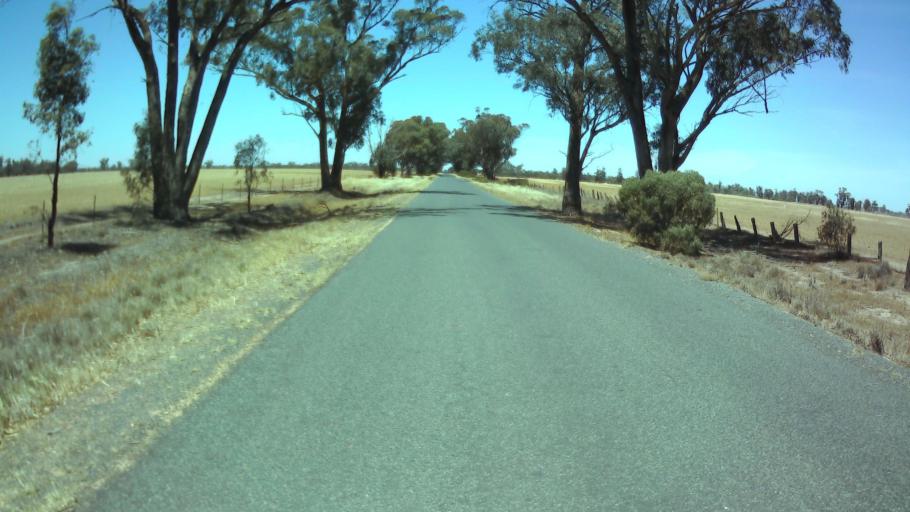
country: AU
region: New South Wales
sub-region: Weddin
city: Grenfell
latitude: -34.0198
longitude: 147.7929
